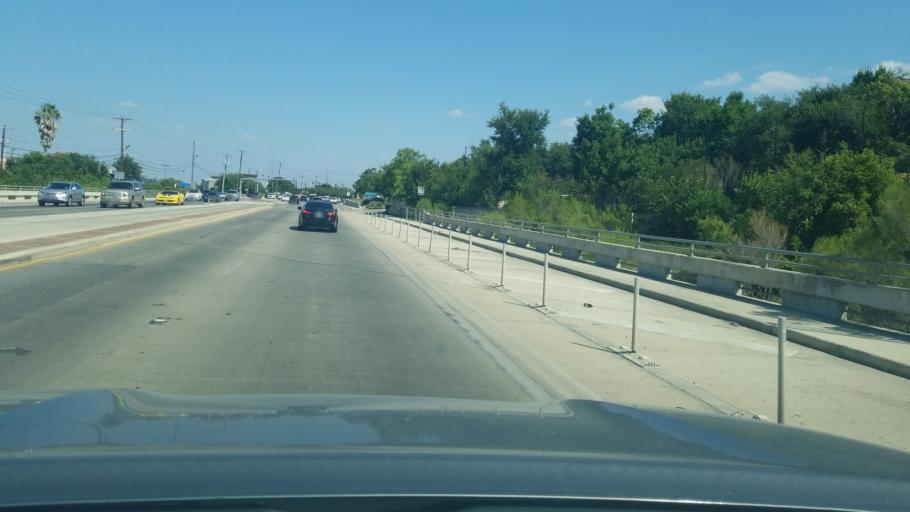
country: US
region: Texas
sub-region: Bexar County
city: Hollywood Park
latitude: 29.6226
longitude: -98.5156
